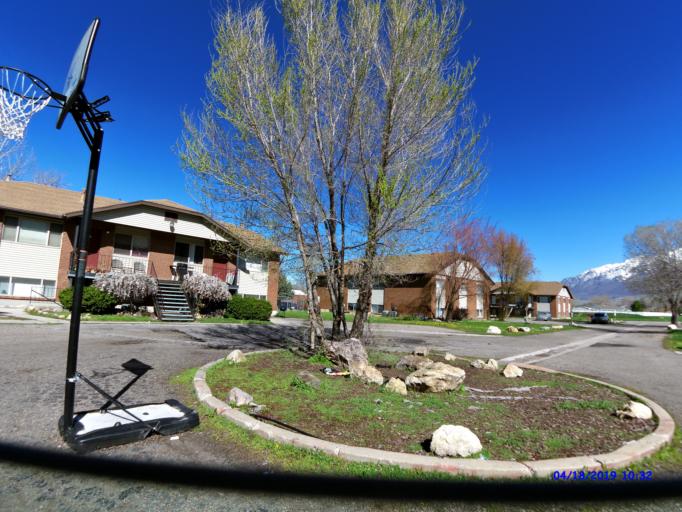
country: US
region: Utah
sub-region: Weber County
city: Harrisville
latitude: 41.2713
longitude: -111.9672
